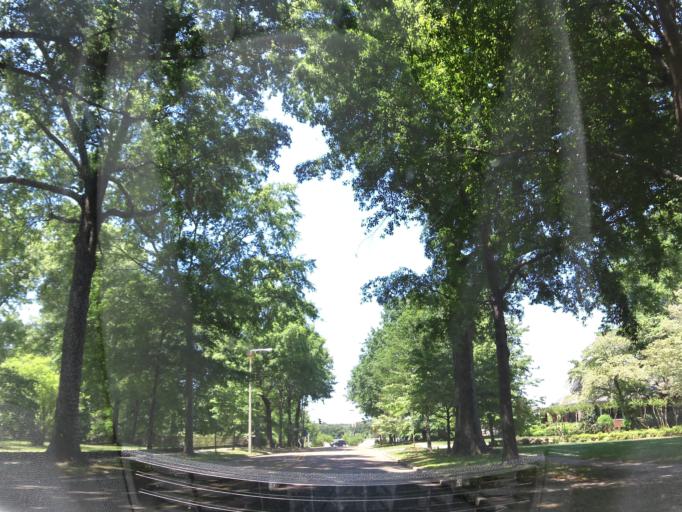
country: US
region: Mississippi
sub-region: Lafayette County
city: Oxford
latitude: 34.3720
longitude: -89.5175
